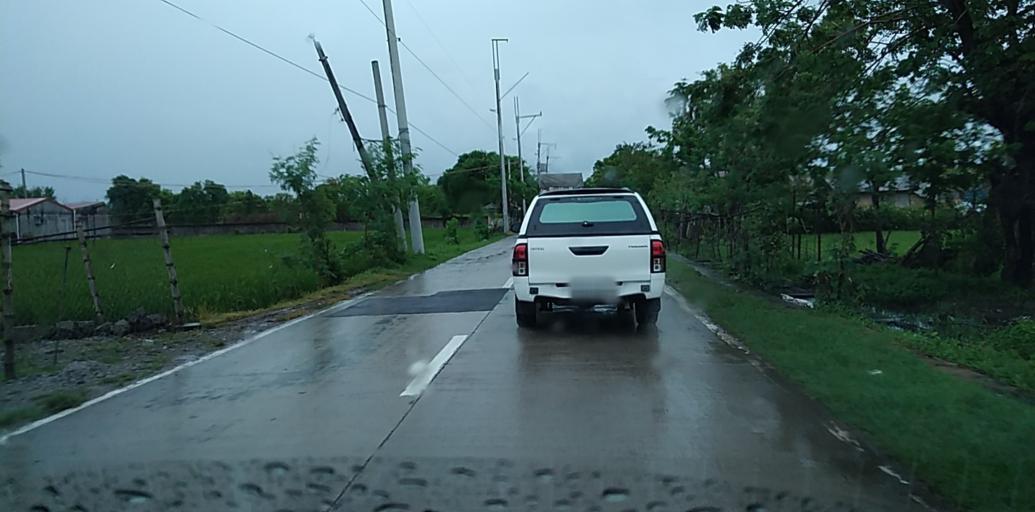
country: PH
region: Central Luzon
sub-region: Province of Pampanga
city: Salapungan
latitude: 15.1361
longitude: 120.9344
